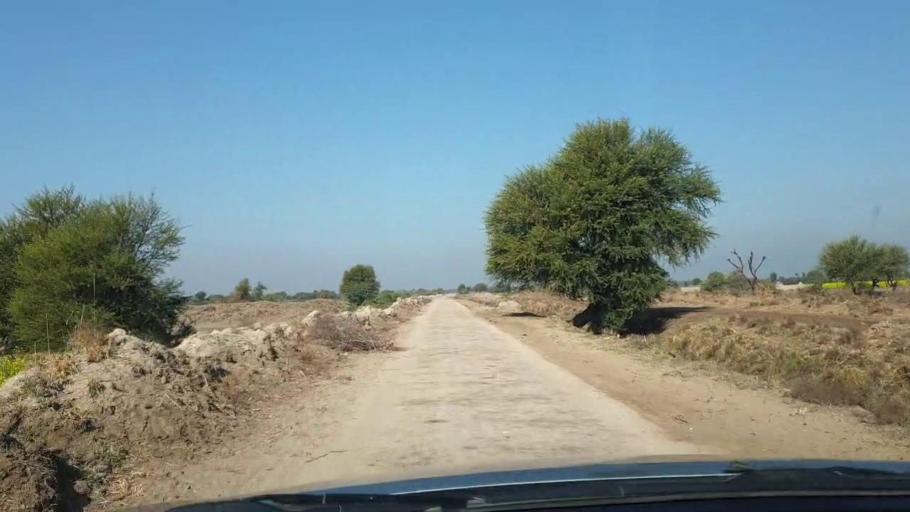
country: PK
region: Sindh
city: Jhol
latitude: 25.8857
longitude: 68.8982
